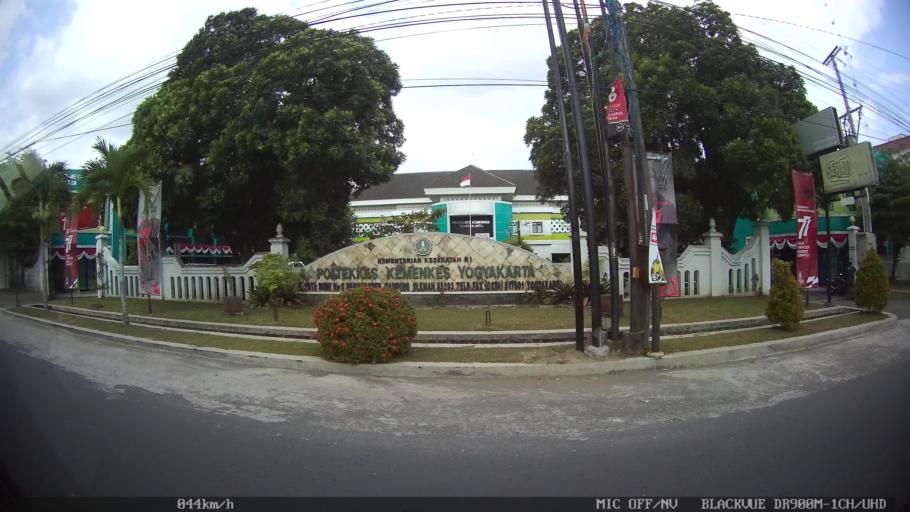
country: ID
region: Daerah Istimewa Yogyakarta
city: Yogyakarta
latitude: -7.7815
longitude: 110.3428
